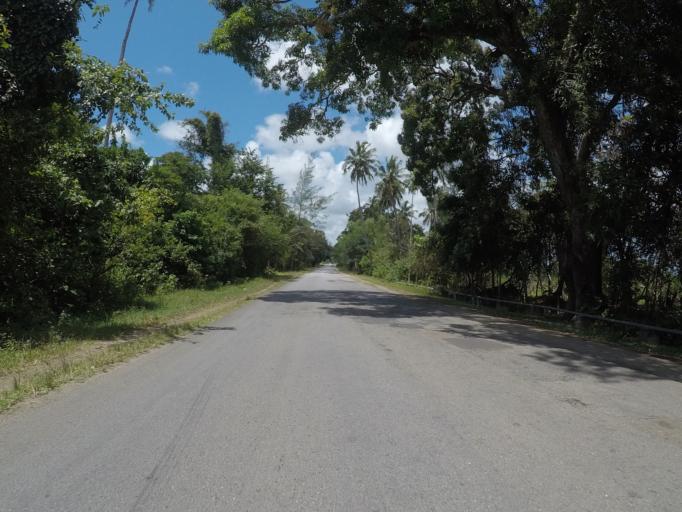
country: TZ
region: Zanzibar Central/South
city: Nganane
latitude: -6.2835
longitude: 39.4356
